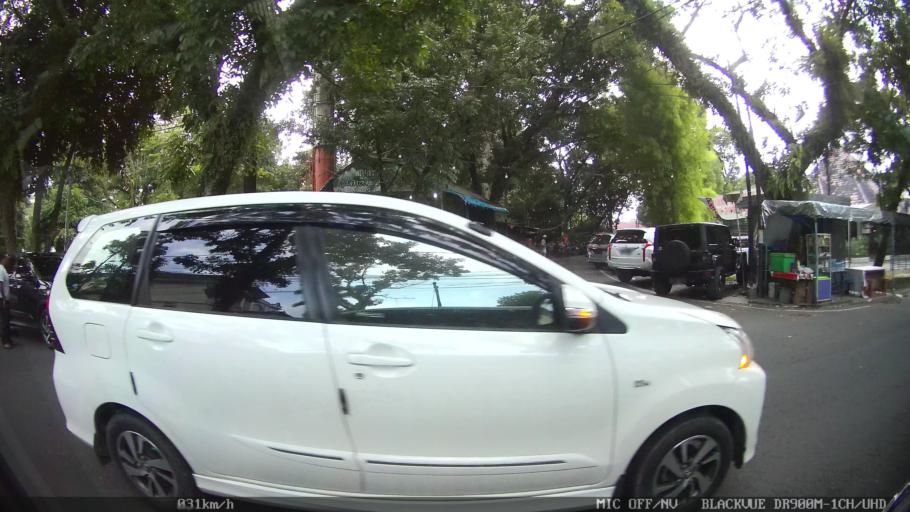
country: ID
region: North Sumatra
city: Medan
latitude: 3.5777
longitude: 98.6696
